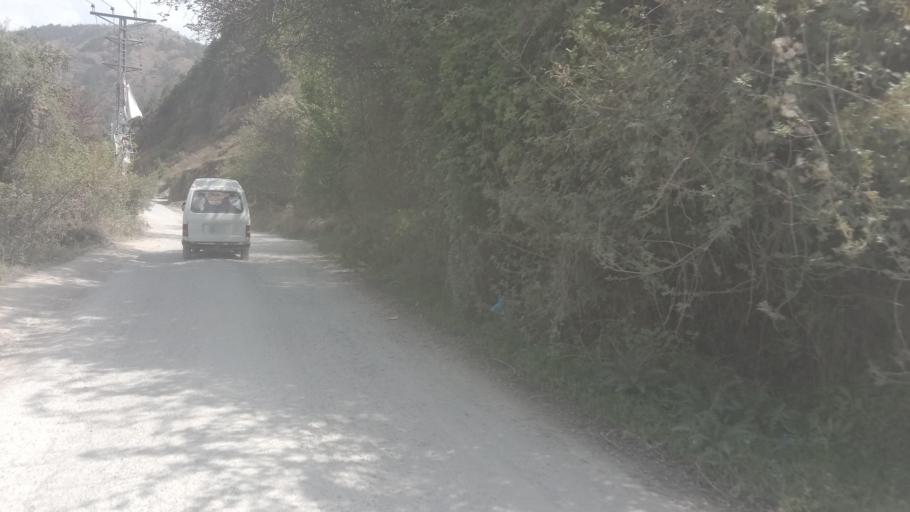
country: PK
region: Khyber Pakhtunkhwa
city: Abbottabad
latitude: 34.1612
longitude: 73.2754
